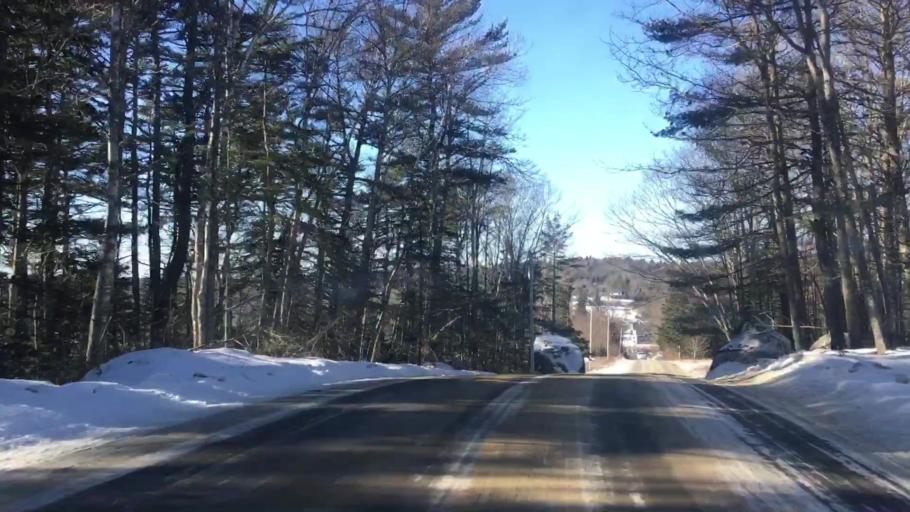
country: US
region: Maine
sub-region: Hancock County
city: Sedgwick
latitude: 44.3440
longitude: -68.6785
